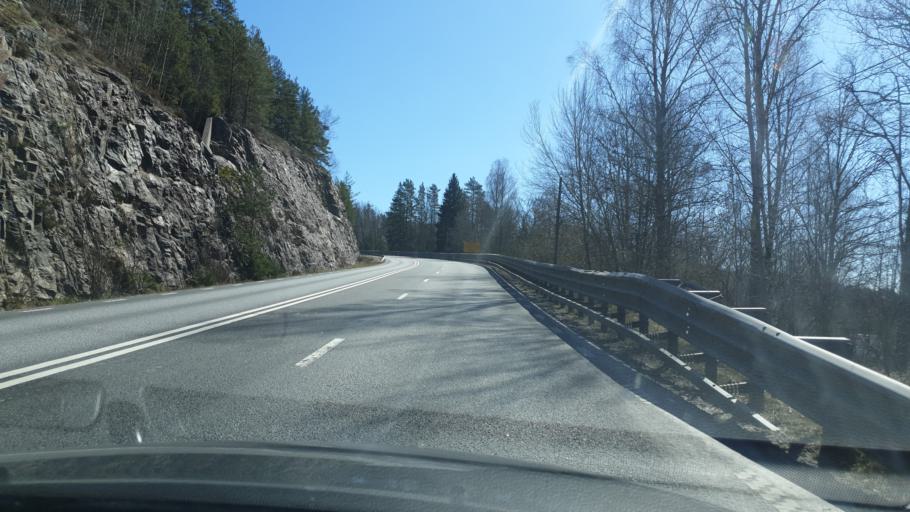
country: SE
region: Vaestra Goetaland
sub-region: Tanums Kommun
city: Tanumshede
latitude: 58.7957
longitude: 11.5715
